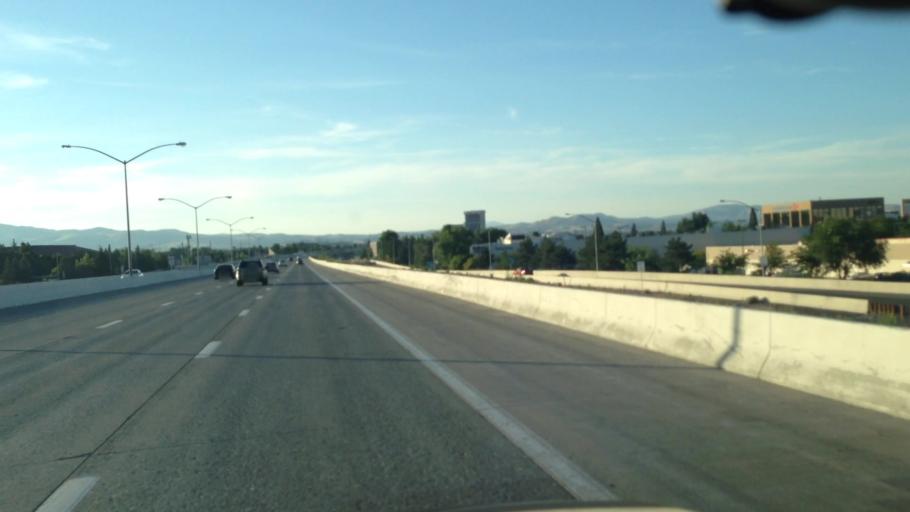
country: US
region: Nevada
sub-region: Washoe County
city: Reno
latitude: 39.4680
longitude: -119.7882
